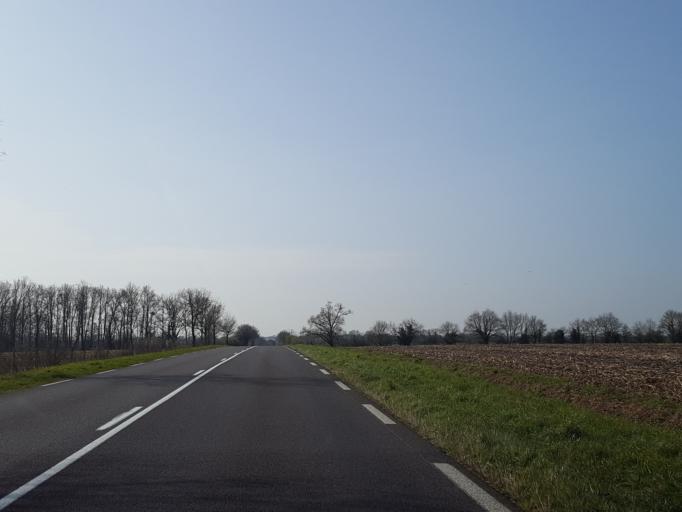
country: FR
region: Pays de la Loire
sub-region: Departement de la Vendee
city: Les Lucs-sur-Boulogne
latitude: 46.8724
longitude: -1.4996
